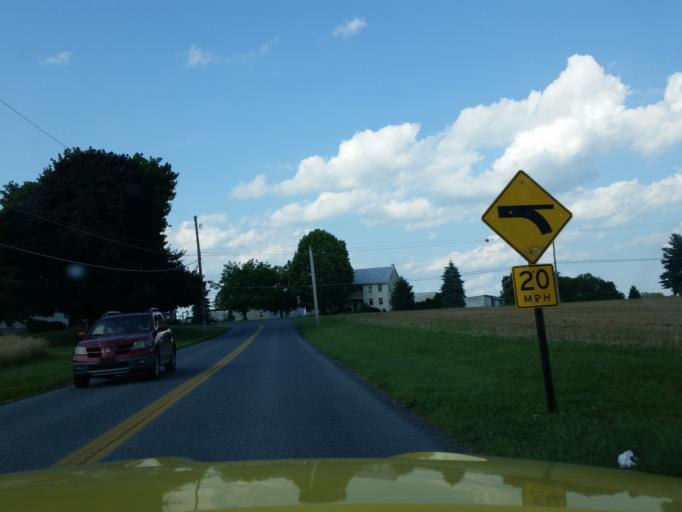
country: US
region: Pennsylvania
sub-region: Lebanon County
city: Jonestown
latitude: 40.4017
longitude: -76.5169
